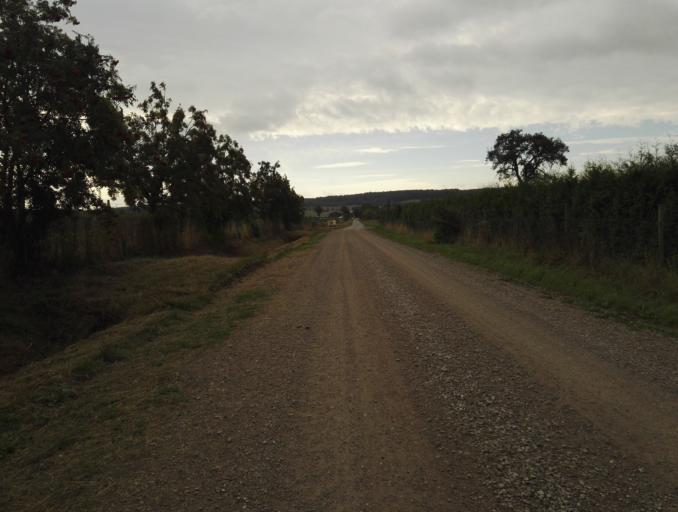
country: DE
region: Lower Saxony
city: Schellerten
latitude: 52.1415
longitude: 10.0648
